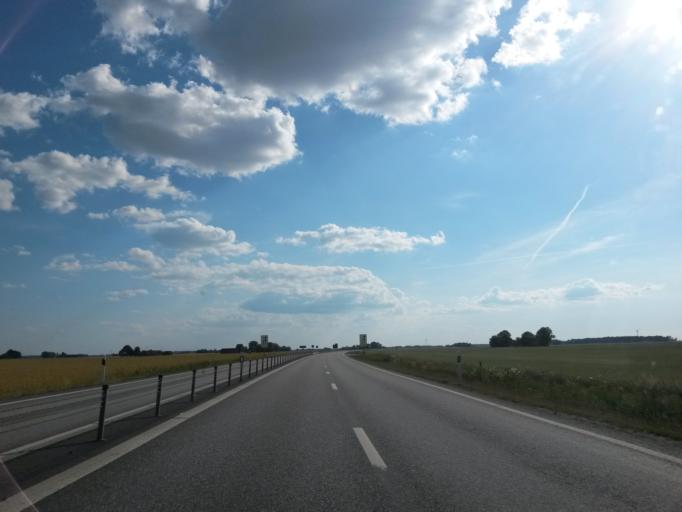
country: SE
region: Vaestra Goetaland
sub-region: Vara Kommun
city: Kvanum
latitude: 58.3219
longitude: 13.1274
